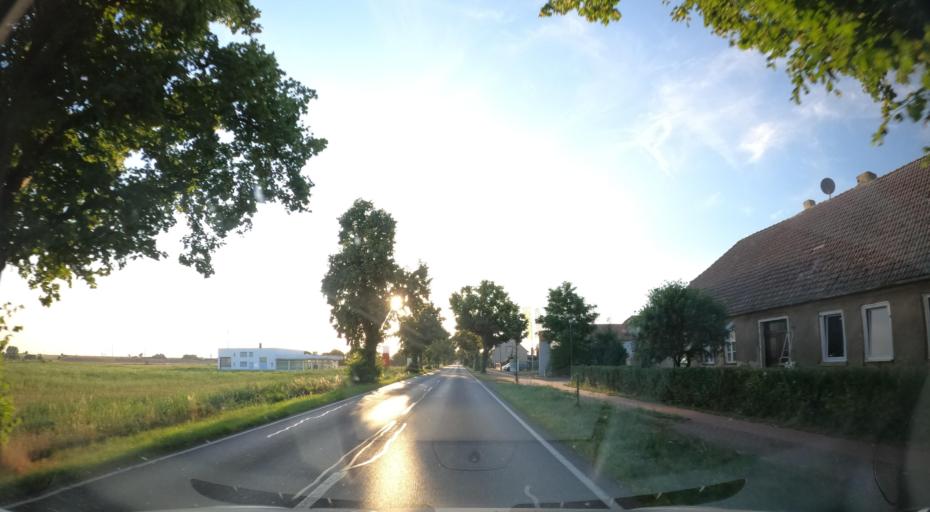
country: DE
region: Brandenburg
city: Brussow
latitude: 53.4567
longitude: 14.1951
